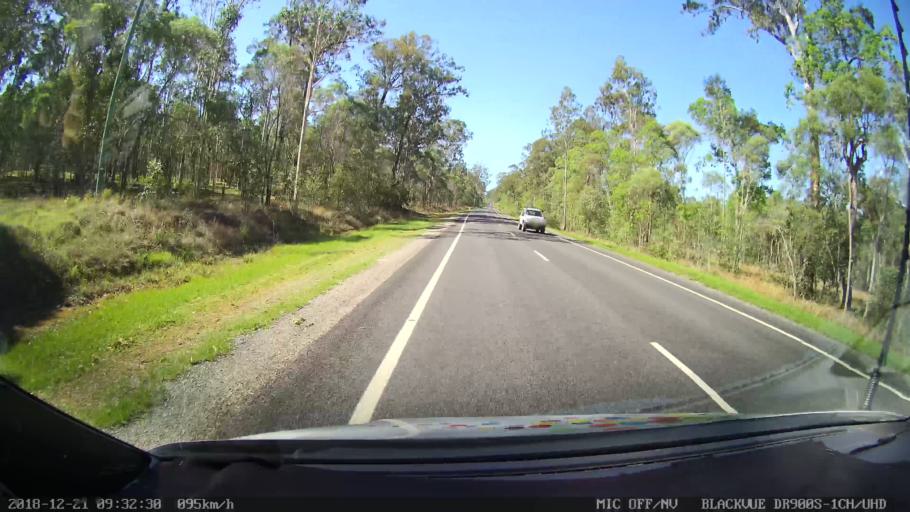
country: AU
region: New South Wales
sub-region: Clarence Valley
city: Maclean
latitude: -29.4713
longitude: 152.9782
